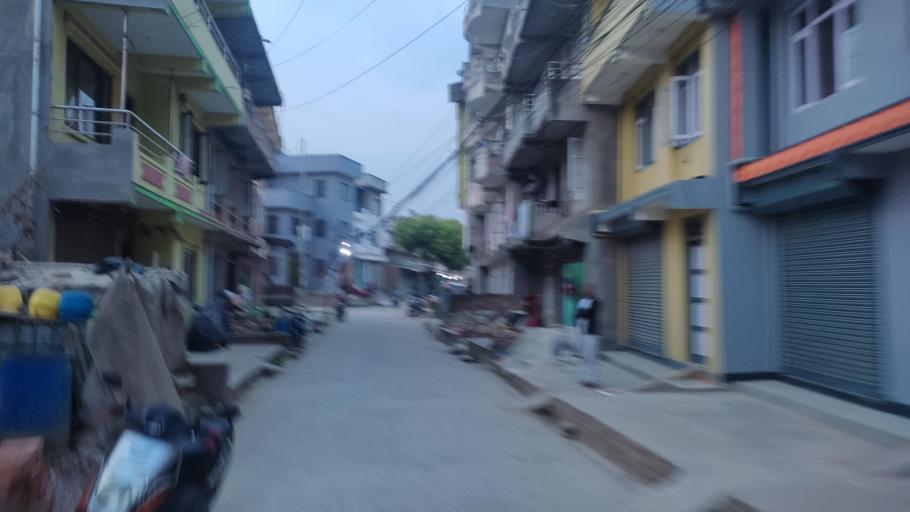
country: NP
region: Central Region
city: Kirtipur
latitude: 27.6711
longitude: 85.2764
